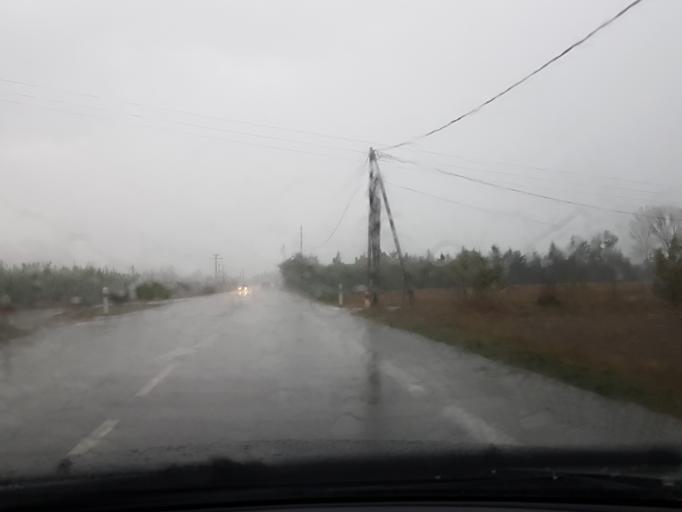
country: FR
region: Provence-Alpes-Cote d'Azur
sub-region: Departement du Vaucluse
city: Pernes-les-Fontaines
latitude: 43.9948
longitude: 5.0113
